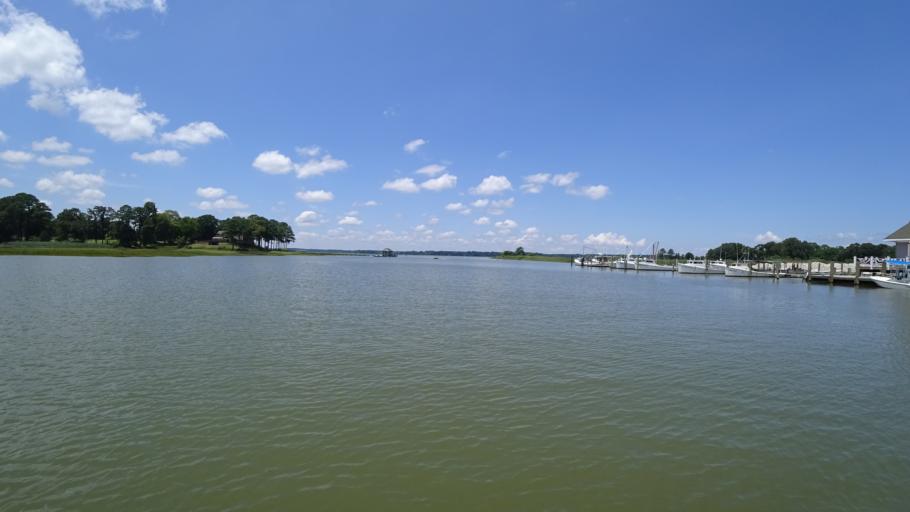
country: US
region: Virginia
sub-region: Isle of Wight County
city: Carrollton
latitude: 36.9976
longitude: -76.5664
